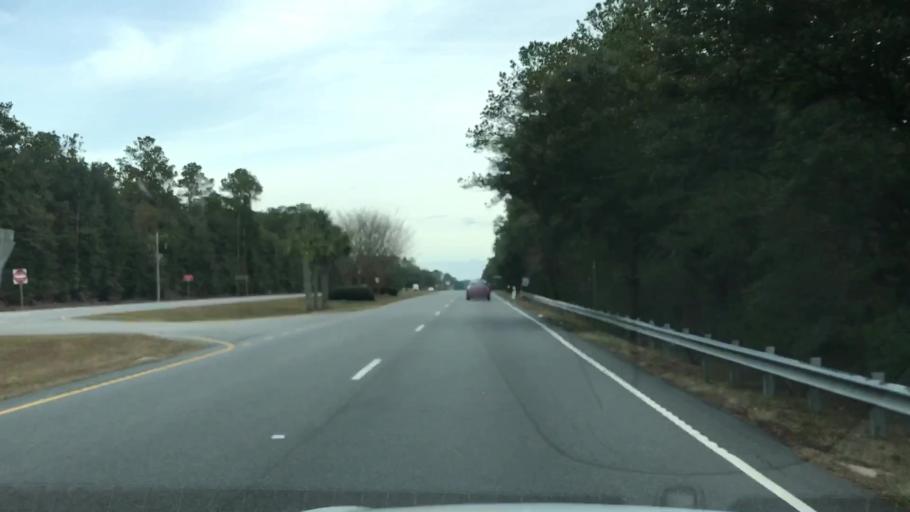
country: US
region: South Carolina
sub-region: Georgetown County
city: Georgetown
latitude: 33.2172
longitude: -79.3799
